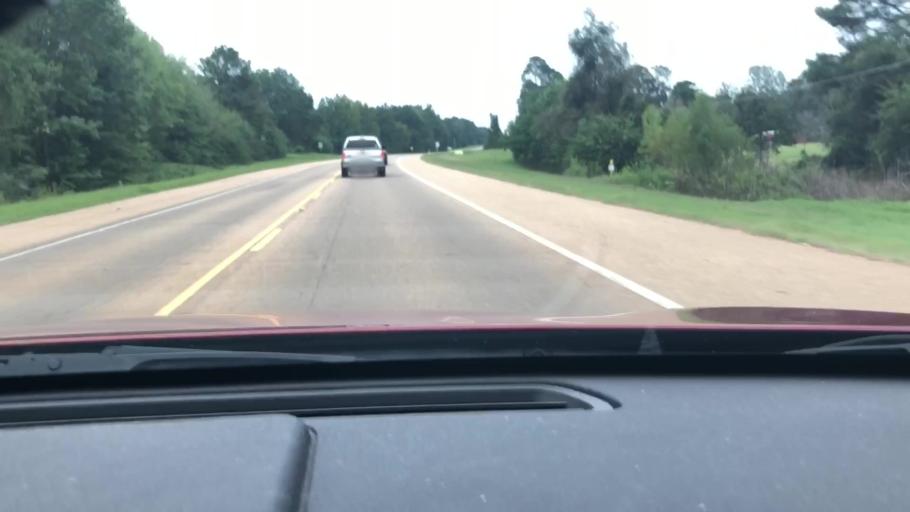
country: US
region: Arkansas
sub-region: Lafayette County
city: Stamps
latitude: 33.3649
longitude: -93.4772
